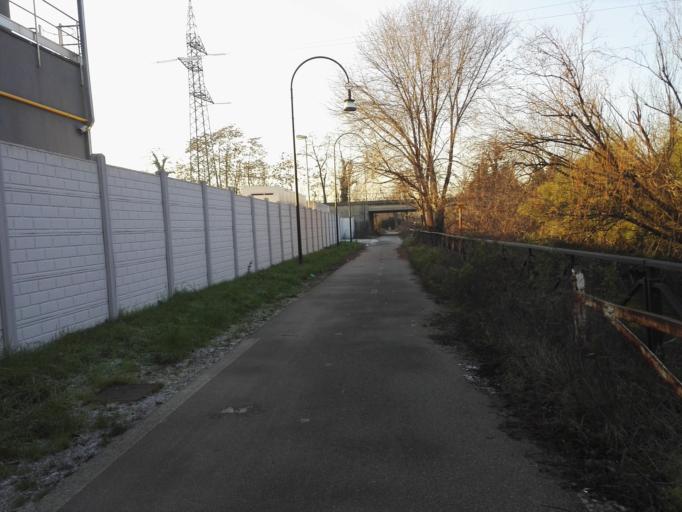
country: IT
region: Lombardy
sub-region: Citta metropolitana di Milano
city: Cologno Monzese
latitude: 45.5181
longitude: 9.2642
